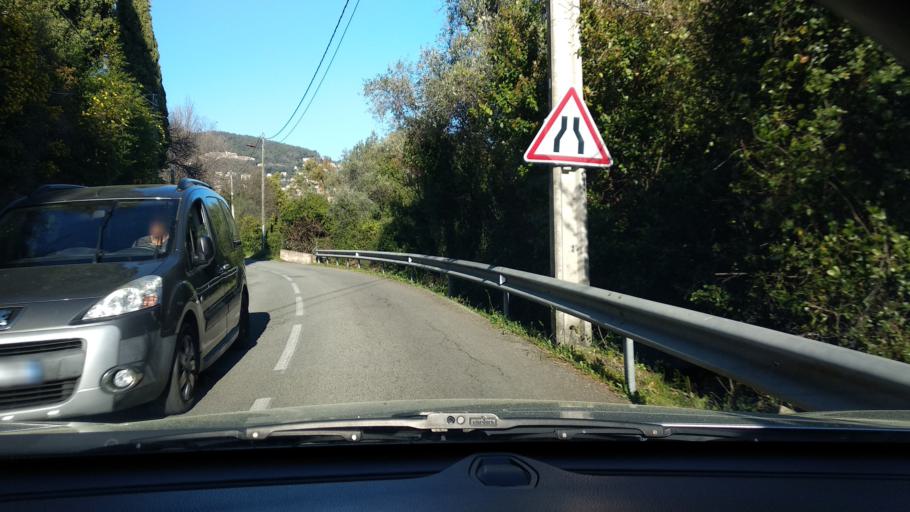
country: FR
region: Provence-Alpes-Cote d'Azur
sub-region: Departement des Alpes-Maritimes
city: Peymeinade
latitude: 43.6474
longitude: 6.8967
